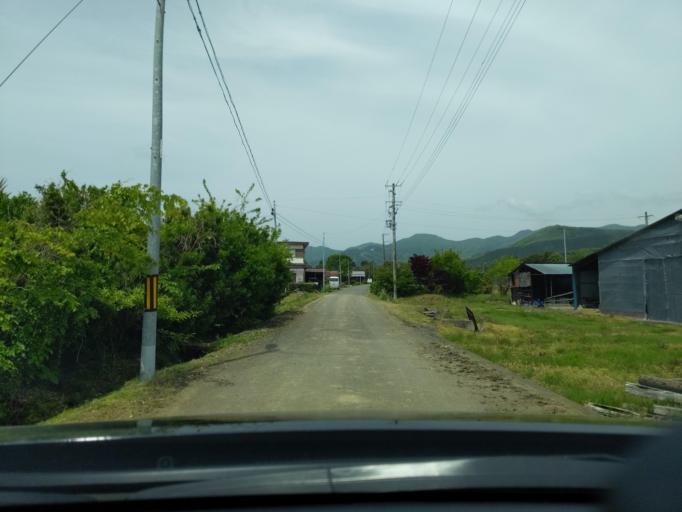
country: JP
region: Fukushima
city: Koriyama
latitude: 37.4058
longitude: 140.2610
